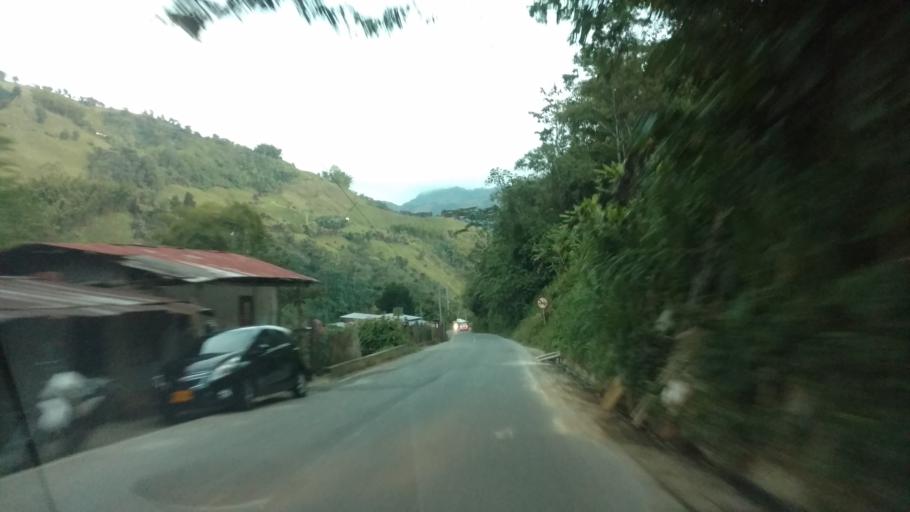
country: CO
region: Caldas
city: Aranzazu
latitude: 5.2629
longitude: -75.5001
